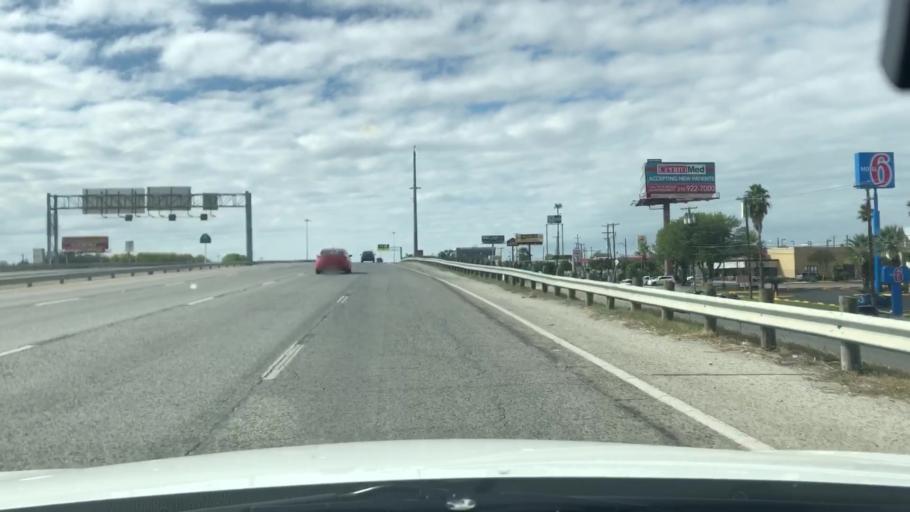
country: US
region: Texas
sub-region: Bexar County
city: Lackland Air Force Base
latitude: 29.4030
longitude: -98.6264
